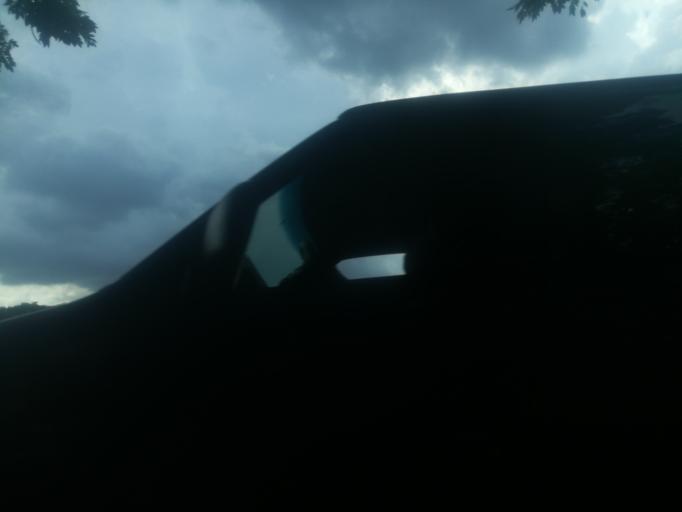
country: NG
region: Oyo
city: Ibadan
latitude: 7.4405
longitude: 3.9034
